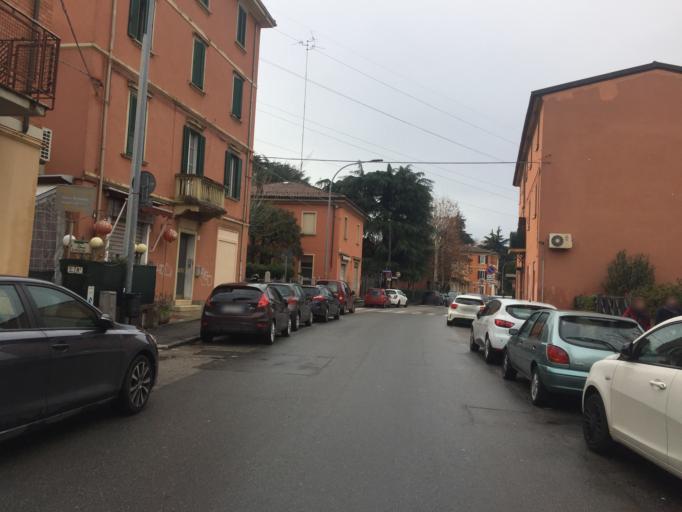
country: IT
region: Emilia-Romagna
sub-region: Provincia di Bologna
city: Casalecchio di Reno
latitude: 44.5078
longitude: 11.2975
